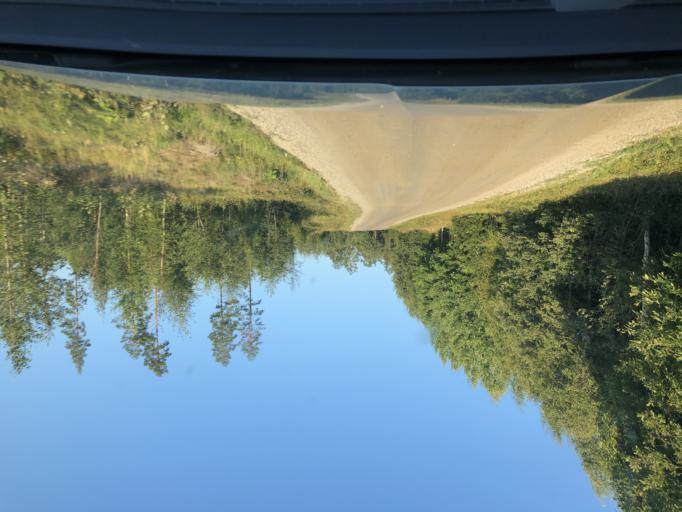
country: SE
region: Vaesternorrland
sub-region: Kramfors Kommun
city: Bollstabruk
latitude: 63.0535
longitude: 17.7090
